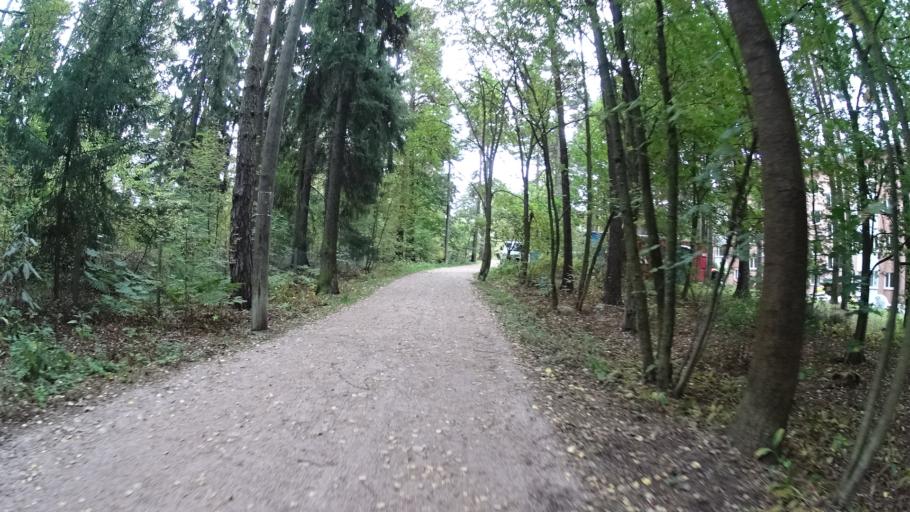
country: FI
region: Uusimaa
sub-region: Helsinki
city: Teekkarikylae
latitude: 60.2003
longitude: 24.8859
